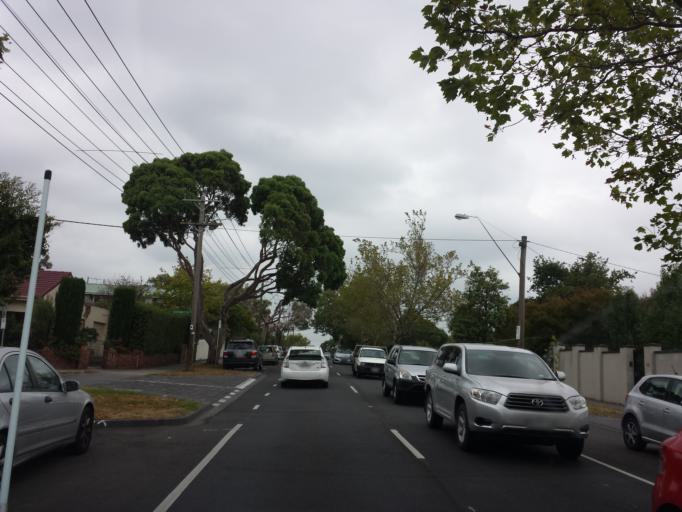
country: AU
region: Victoria
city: Glenferrie
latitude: -37.8323
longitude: 145.0432
